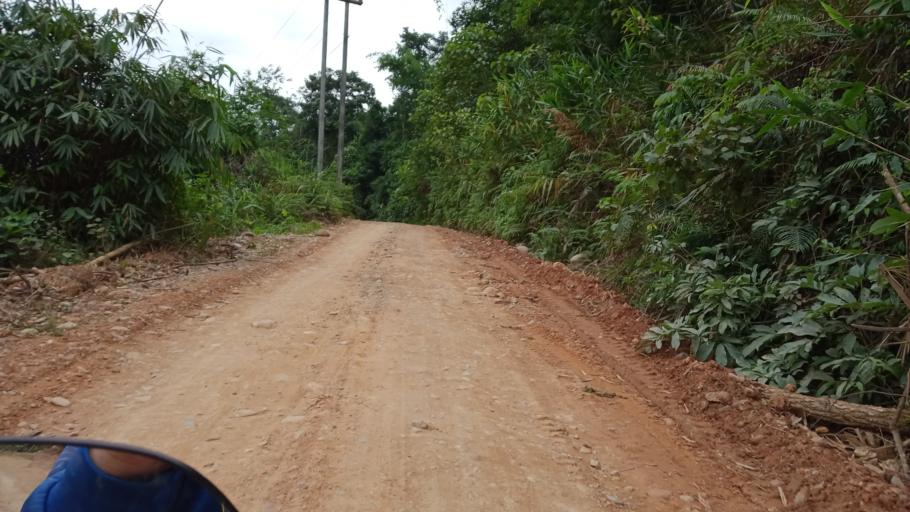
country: LA
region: Xiangkhoang
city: Phonsavan
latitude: 19.0936
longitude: 102.9915
